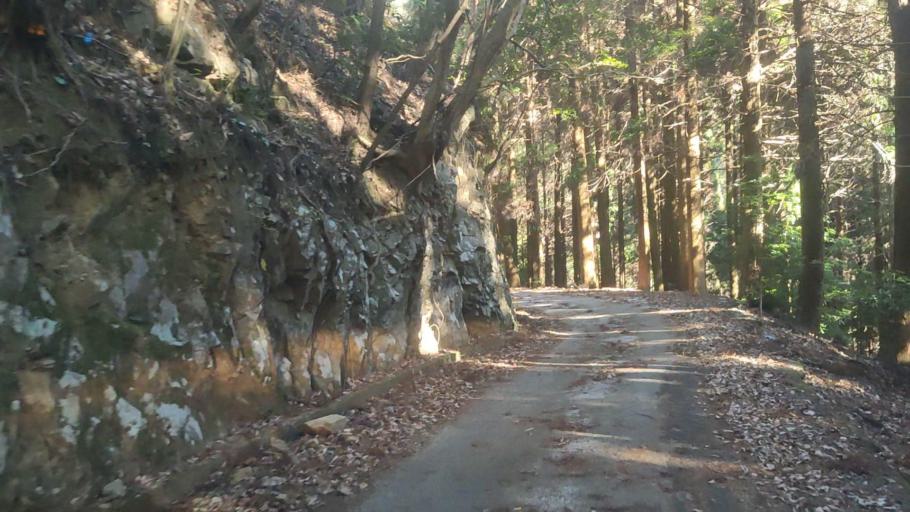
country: JP
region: Oita
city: Saiki
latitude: 32.7850
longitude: 131.8517
